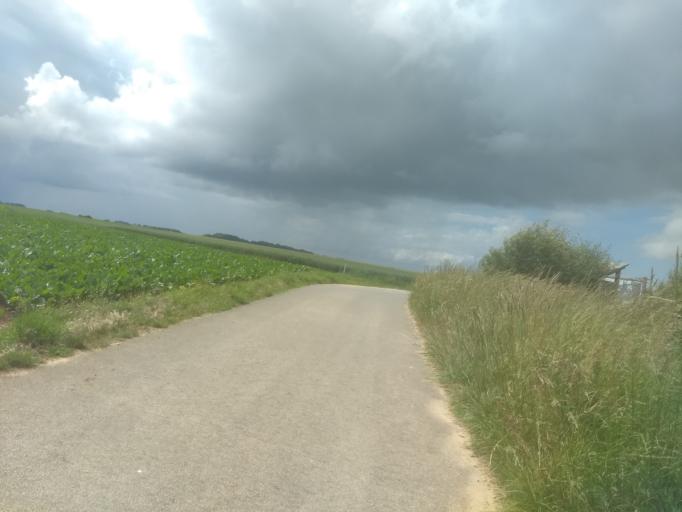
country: FR
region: Nord-Pas-de-Calais
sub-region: Departement du Pas-de-Calais
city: Dainville
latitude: 50.2609
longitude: 2.7073
